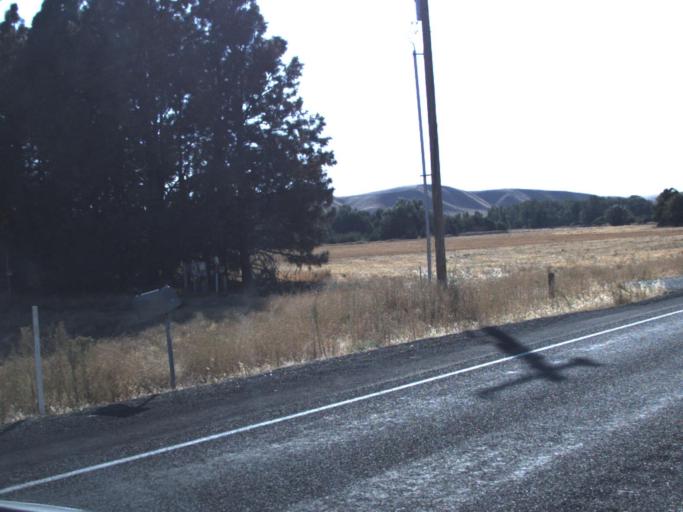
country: US
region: Washington
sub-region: Walla Walla County
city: Waitsburg
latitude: 46.2999
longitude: -118.3718
